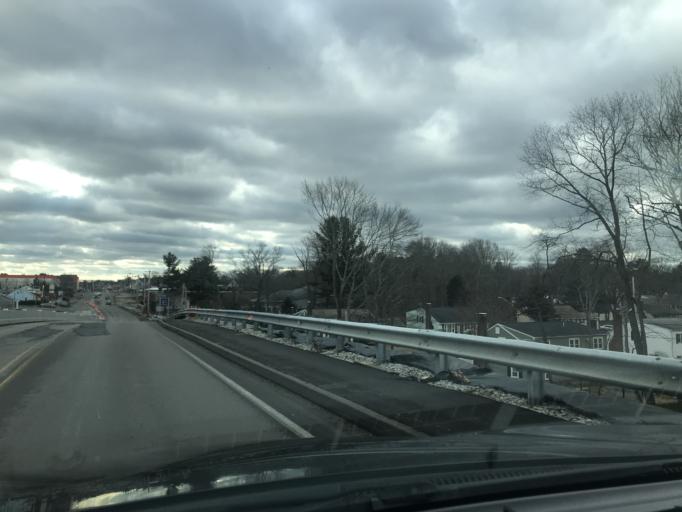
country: US
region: Massachusetts
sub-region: Plymouth County
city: Rockland
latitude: 42.1580
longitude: -70.9552
